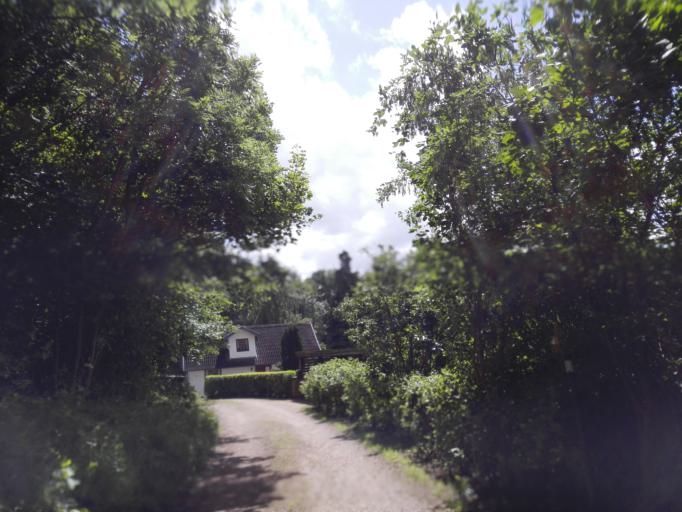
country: DK
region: Capital Region
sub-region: Allerod Kommune
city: Lynge
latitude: 55.8213
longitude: 12.3044
